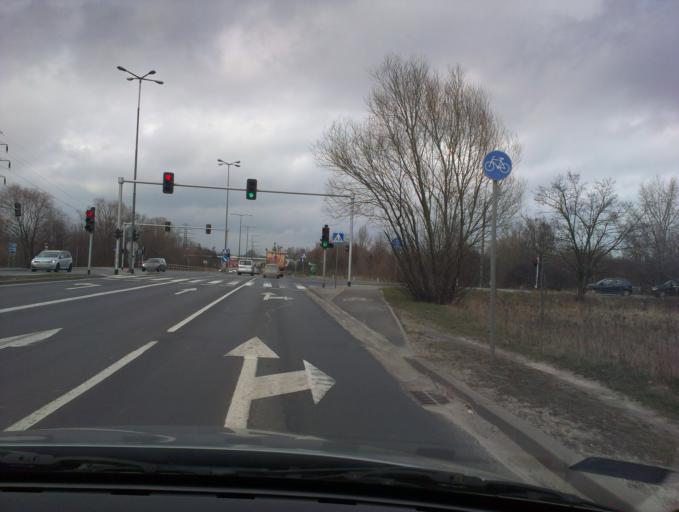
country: PL
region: Greater Poland Voivodeship
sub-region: Poznan
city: Poznan
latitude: 52.3889
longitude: 16.9926
